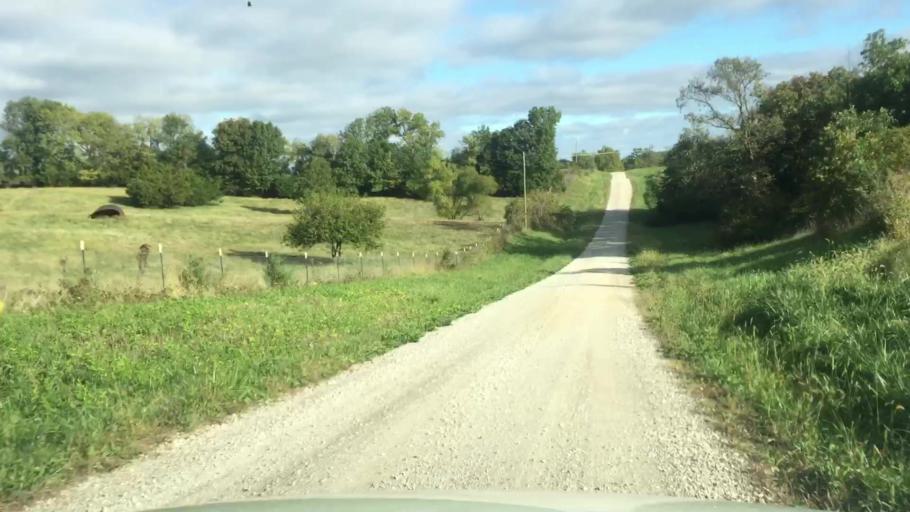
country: US
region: Missouri
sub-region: Howard County
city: New Franklin
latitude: 39.0964
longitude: -92.7795
